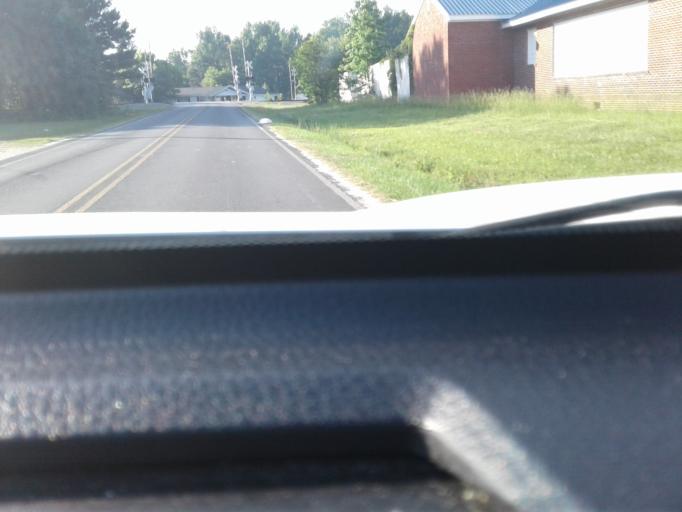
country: US
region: North Carolina
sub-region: Harnett County
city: Dunn
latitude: 35.3431
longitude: -78.5818
